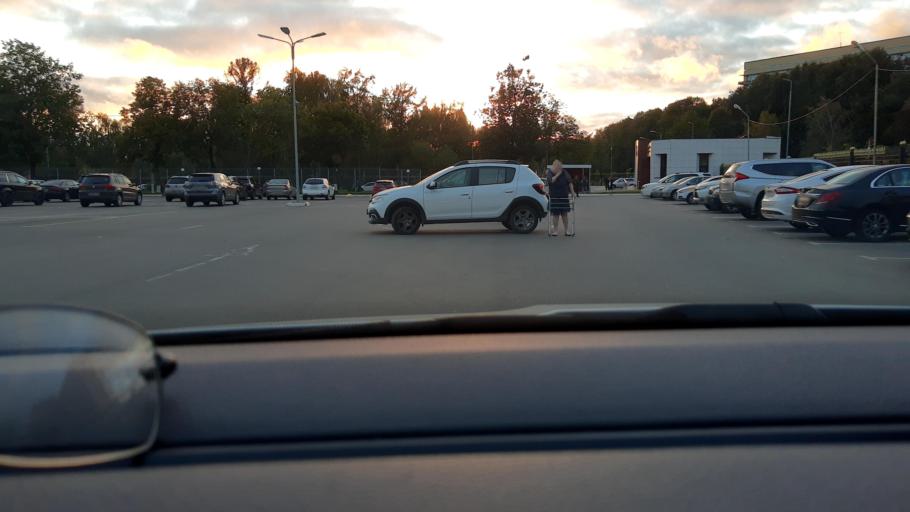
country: RU
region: Moskovskaya
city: Arkhangel'skoye
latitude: 55.8079
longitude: 37.2977
